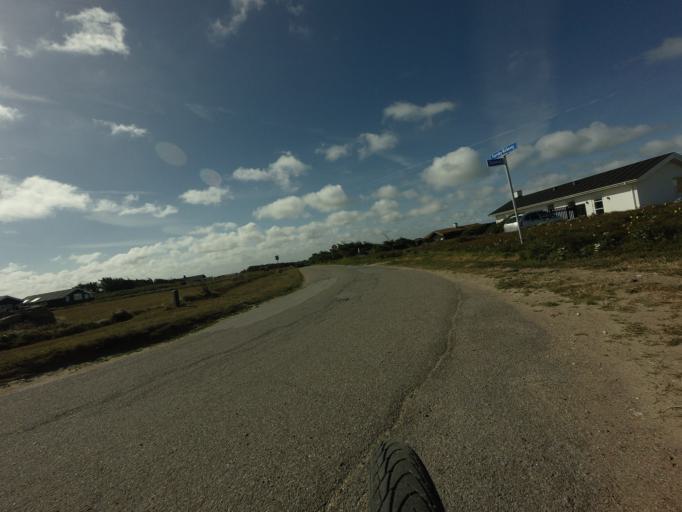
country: DK
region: North Denmark
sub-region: Jammerbugt Kommune
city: Pandrup
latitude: 57.3900
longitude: 9.7287
